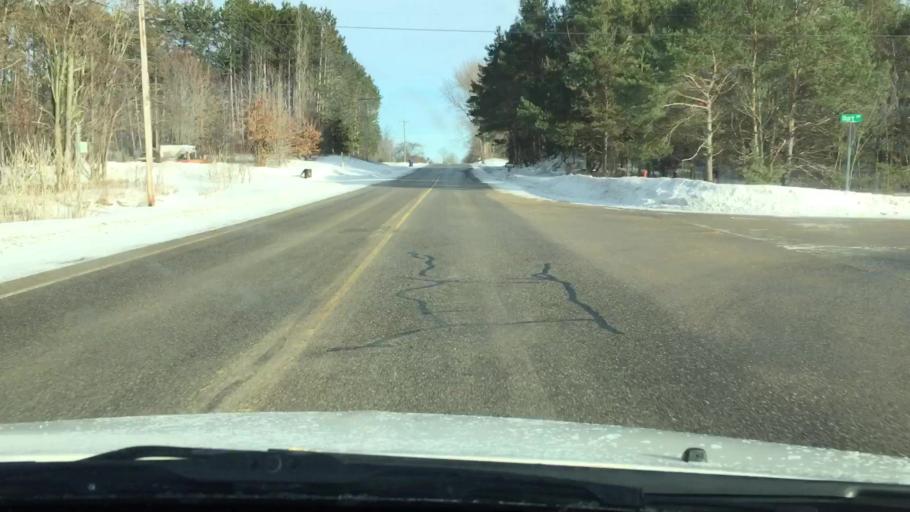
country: US
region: Michigan
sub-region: Kalkaska County
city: Kalkaska
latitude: 44.6408
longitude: -85.2309
